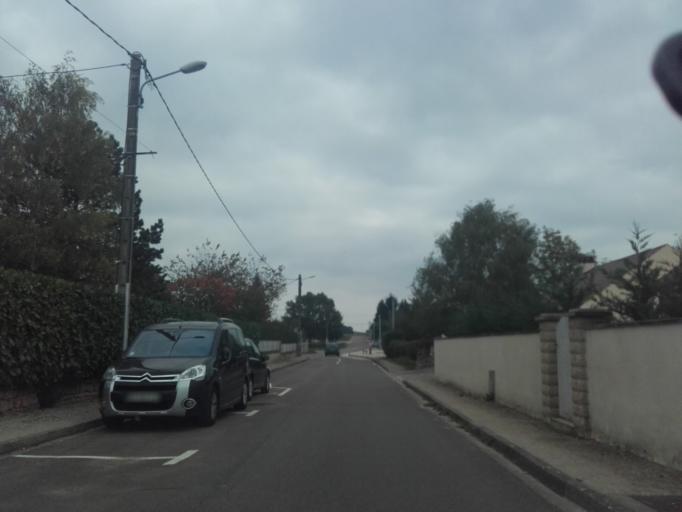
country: FR
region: Bourgogne
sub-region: Departement de Saone-et-Loire
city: Chagny
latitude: 46.8985
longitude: 4.7690
